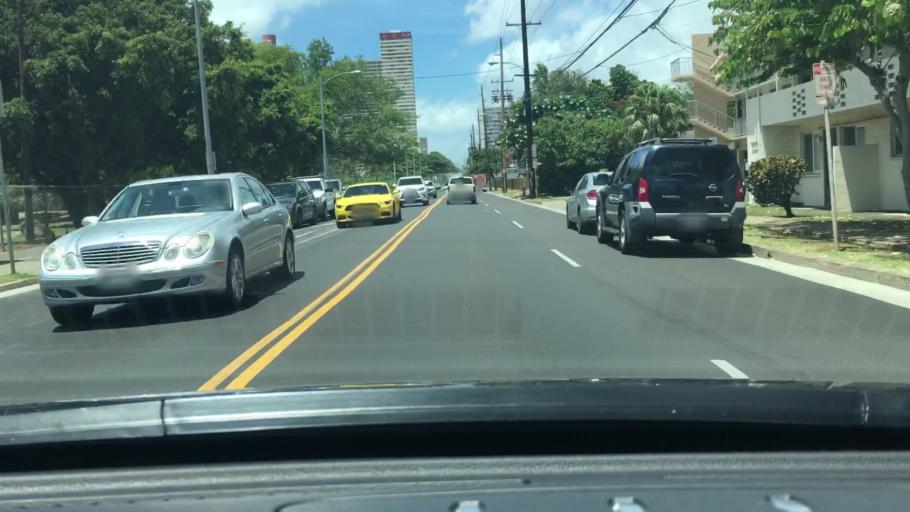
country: US
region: Hawaii
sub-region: Honolulu County
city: Honolulu
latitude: 21.2829
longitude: -157.8183
